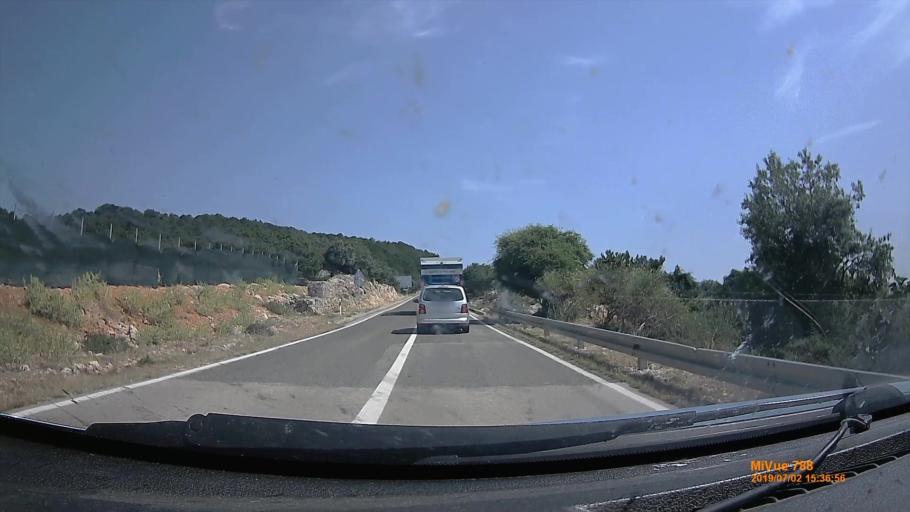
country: HR
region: Primorsko-Goranska
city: Cres
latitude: 44.9815
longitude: 14.4136
